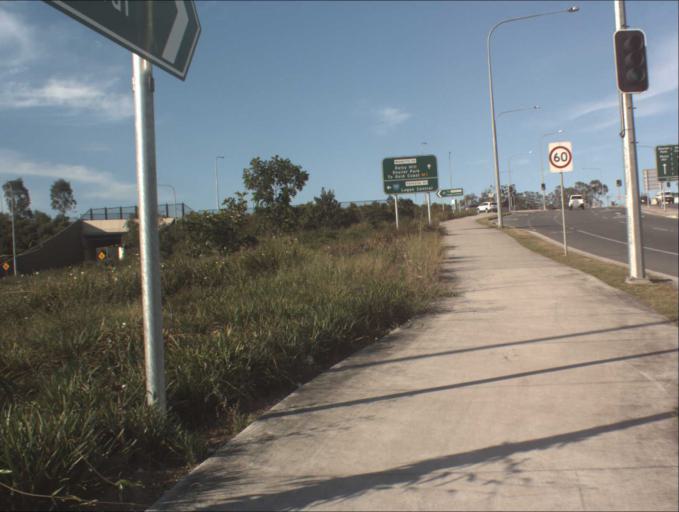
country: AU
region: Queensland
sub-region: Logan
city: Slacks Creek
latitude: -27.6452
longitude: 153.1443
